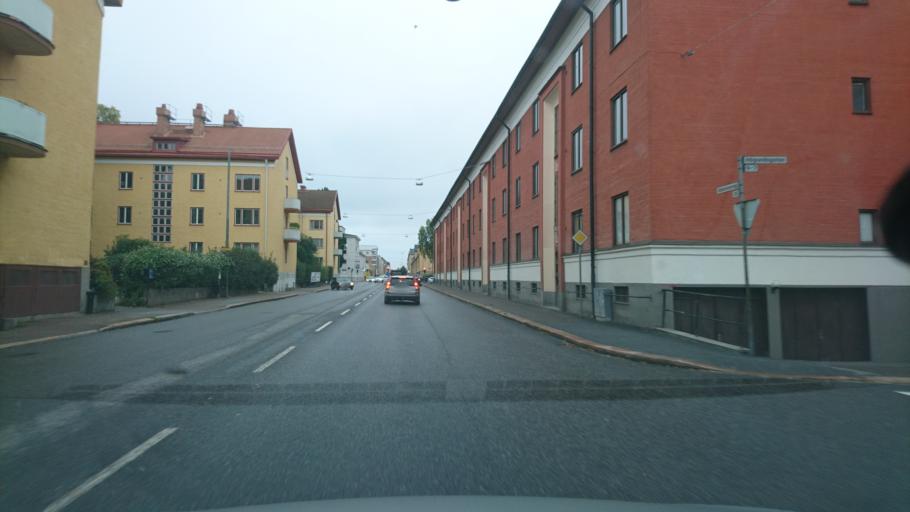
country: SE
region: Uppsala
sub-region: Uppsala Kommun
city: Uppsala
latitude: 59.8653
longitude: 17.6418
